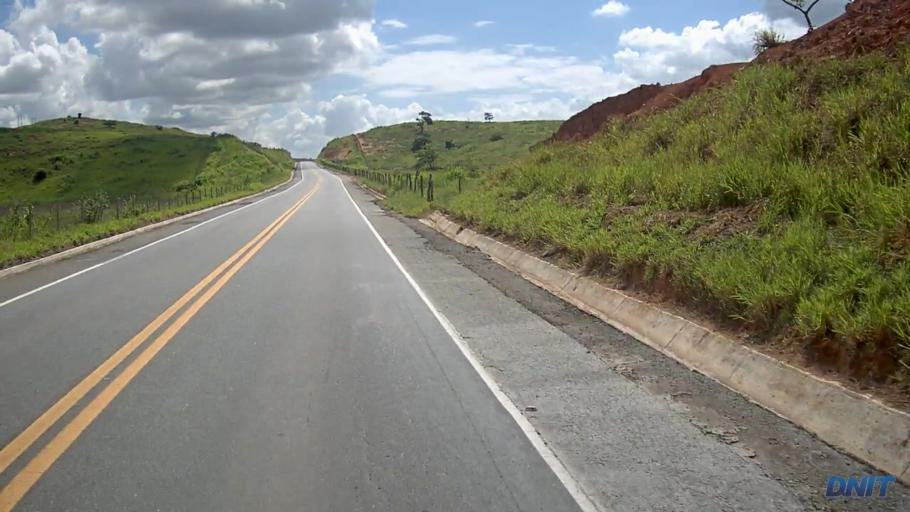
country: BR
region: Minas Gerais
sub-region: Governador Valadares
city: Governador Valadares
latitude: -18.9935
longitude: -42.1175
